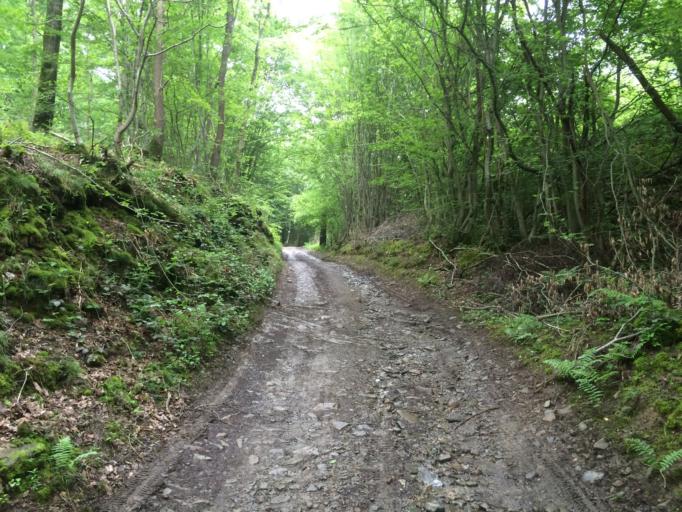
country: BE
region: Wallonia
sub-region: Province de Namur
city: Yvoir
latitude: 50.3256
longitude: 4.9507
